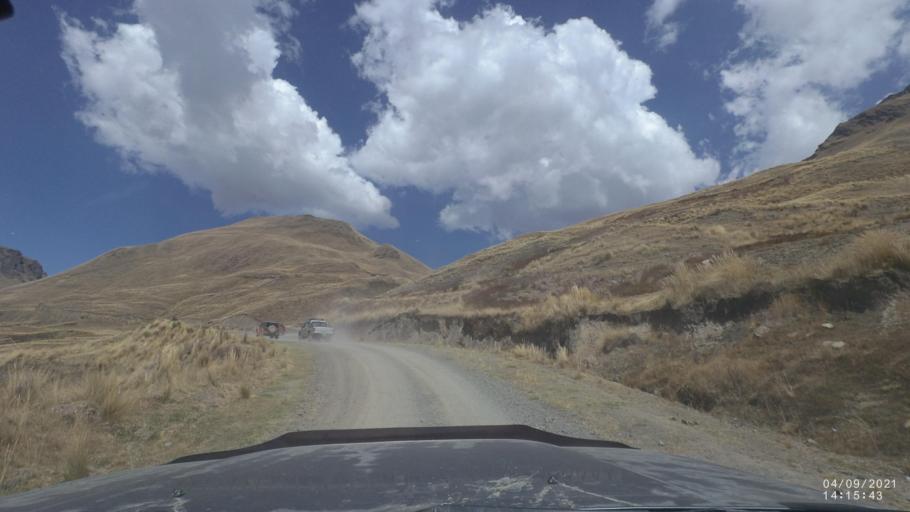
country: BO
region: Cochabamba
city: Sipe Sipe
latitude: -17.2292
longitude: -66.4403
